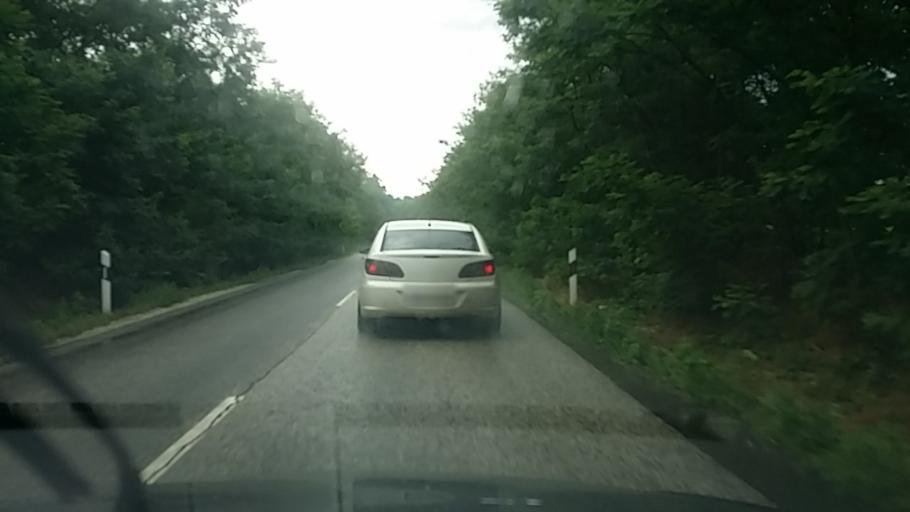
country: HU
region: Pest
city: Ullo
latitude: 47.3514
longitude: 19.3085
